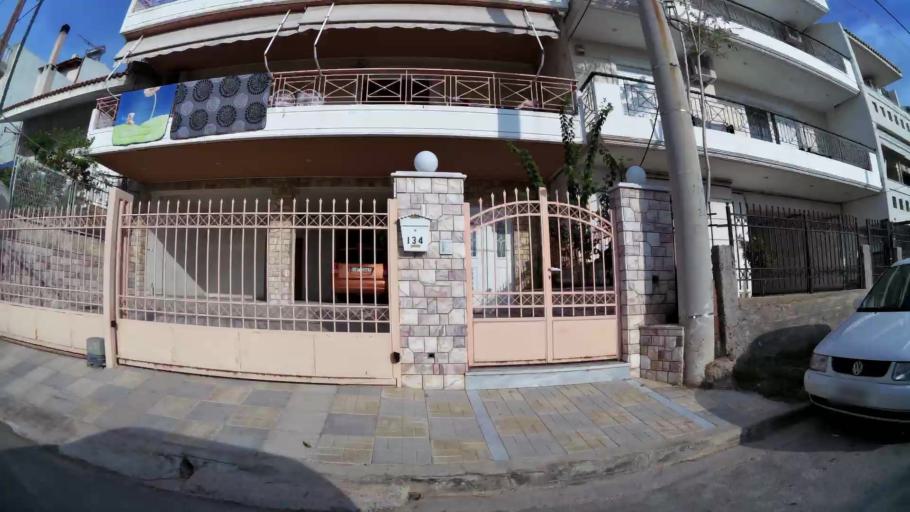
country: GR
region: Attica
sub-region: Nomarchia Athinas
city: Kamateron
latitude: 38.0563
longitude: 23.6954
